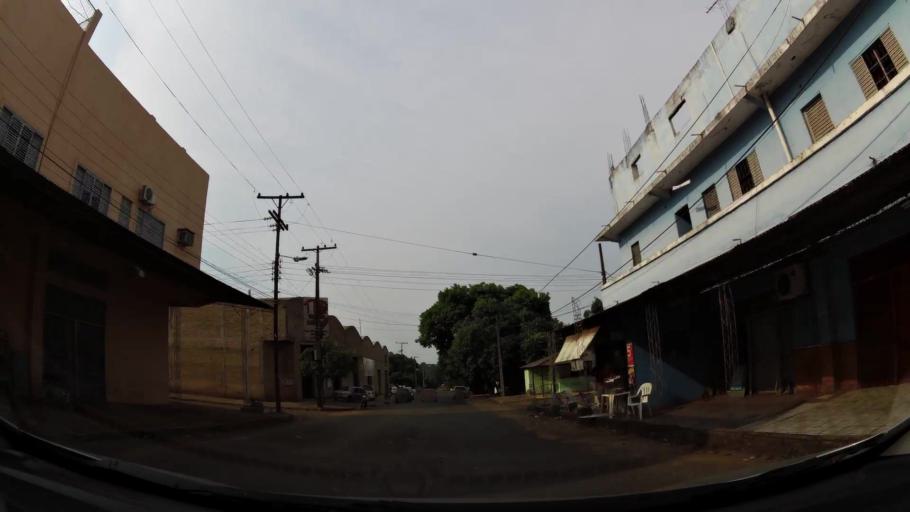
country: PY
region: Alto Parana
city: Ciudad del Este
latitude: -25.4980
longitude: -54.6599
